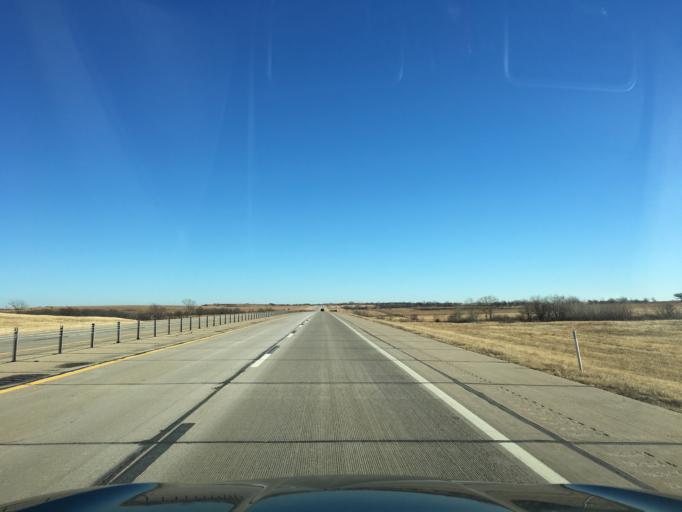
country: US
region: Oklahoma
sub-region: Noble County
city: Perry
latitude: 36.3943
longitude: -97.2158
